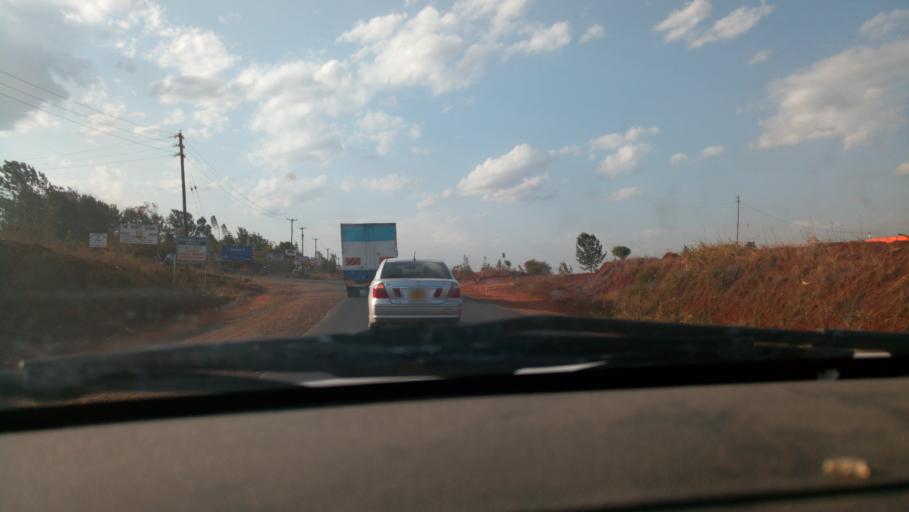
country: KE
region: Murang'a District
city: Maragua
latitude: -0.8018
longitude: 37.1376
